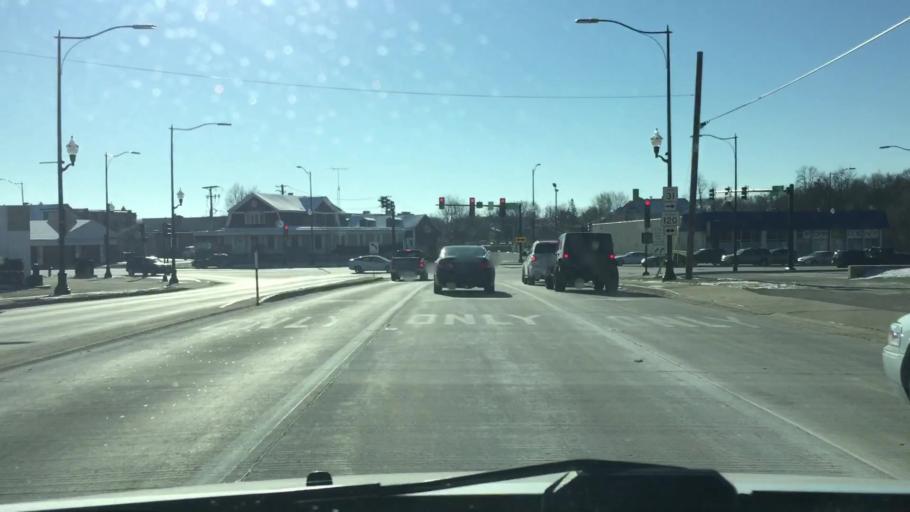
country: US
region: Illinois
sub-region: McHenry County
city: McHenry
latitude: 42.3468
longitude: -88.2674
